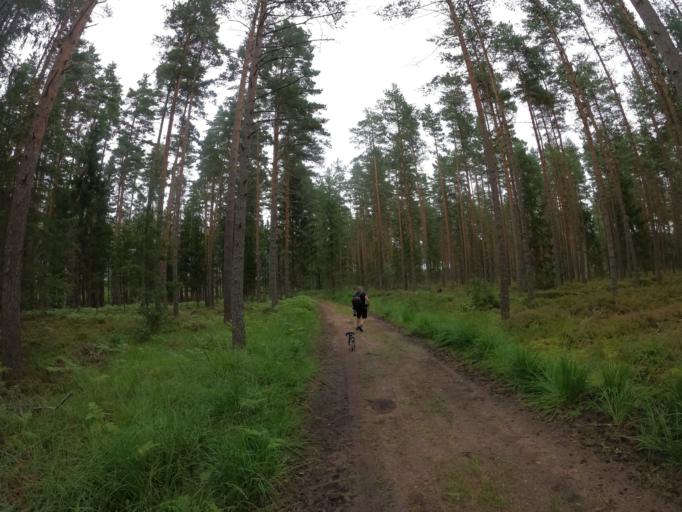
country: LV
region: Kuldigas Rajons
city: Kuldiga
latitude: 57.0410
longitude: 22.0588
